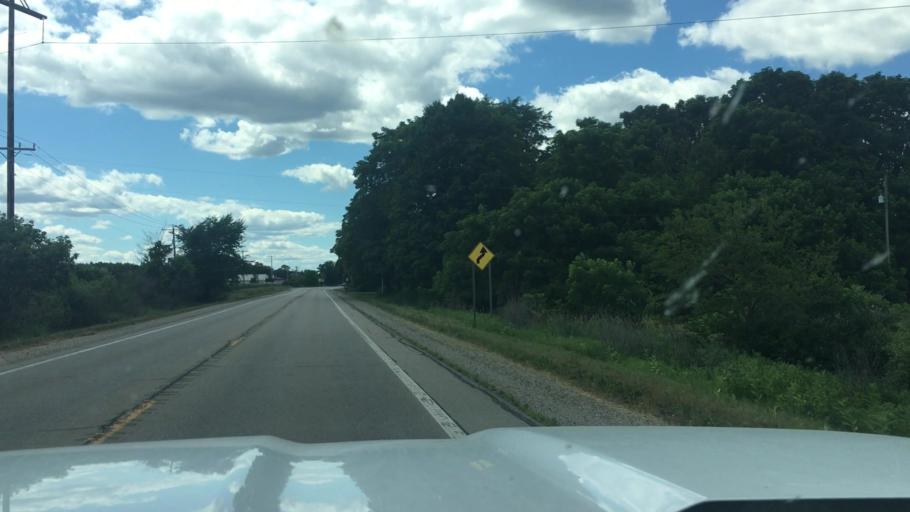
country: US
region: Michigan
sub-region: Montcalm County
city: Greenville
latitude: 43.1705
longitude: -85.2266
